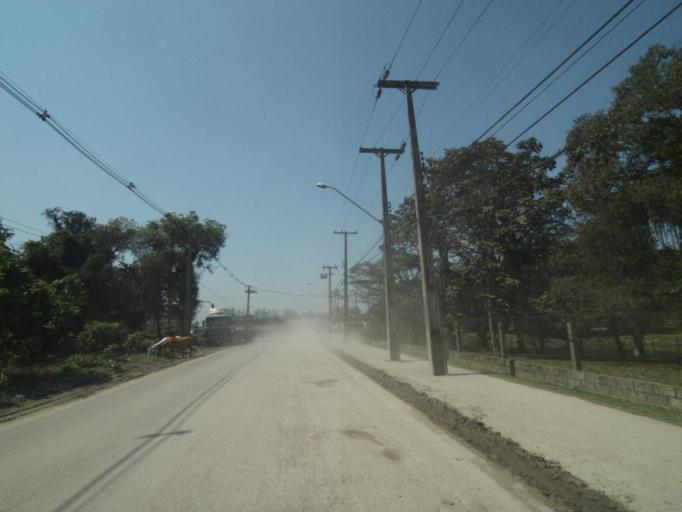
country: BR
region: Parana
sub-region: Paranagua
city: Paranagua
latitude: -25.5457
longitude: -48.5702
